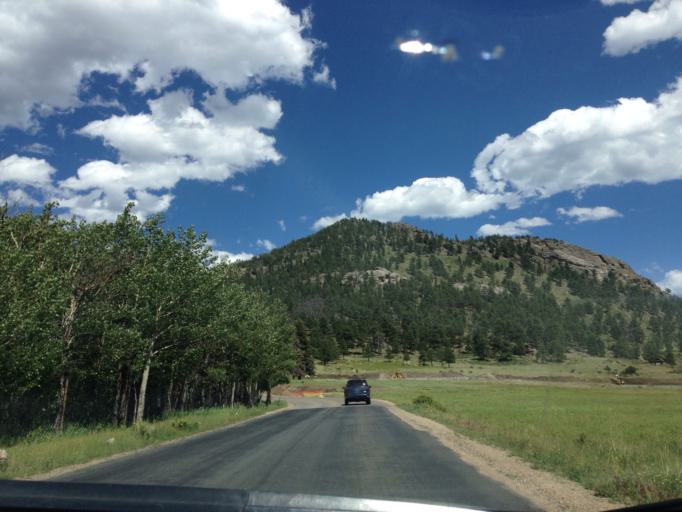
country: US
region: Colorado
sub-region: Larimer County
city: Estes Park
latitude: 40.3579
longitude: -105.5882
